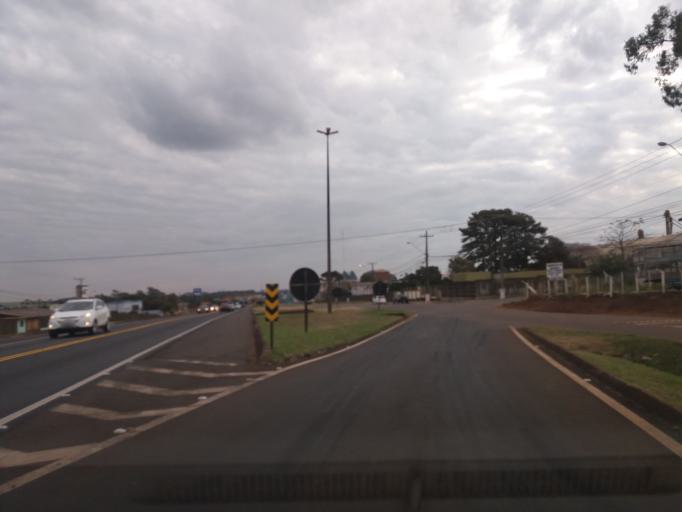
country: BR
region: Parana
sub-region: Cascavel
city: Cascavel
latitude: -24.9841
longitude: -53.4636
